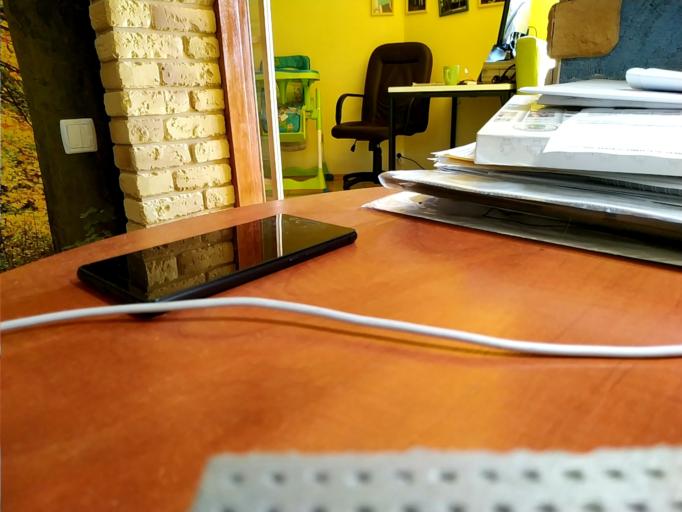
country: RU
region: Tverskaya
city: Kalashnikovo
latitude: 57.3765
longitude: 35.3775
